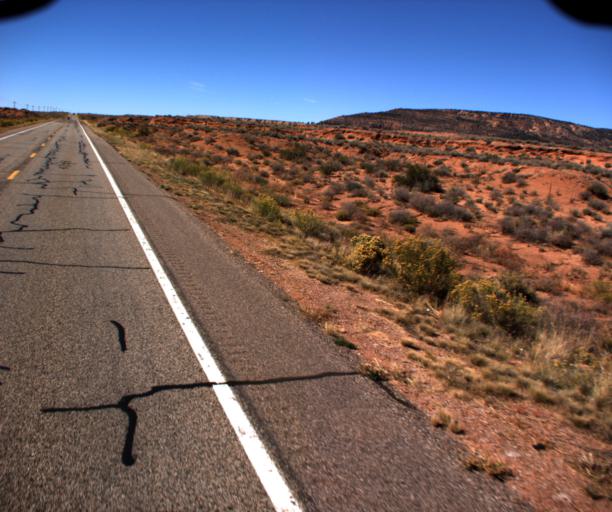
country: US
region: Arizona
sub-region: Coconino County
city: Fredonia
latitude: 36.8640
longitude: -112.7074
